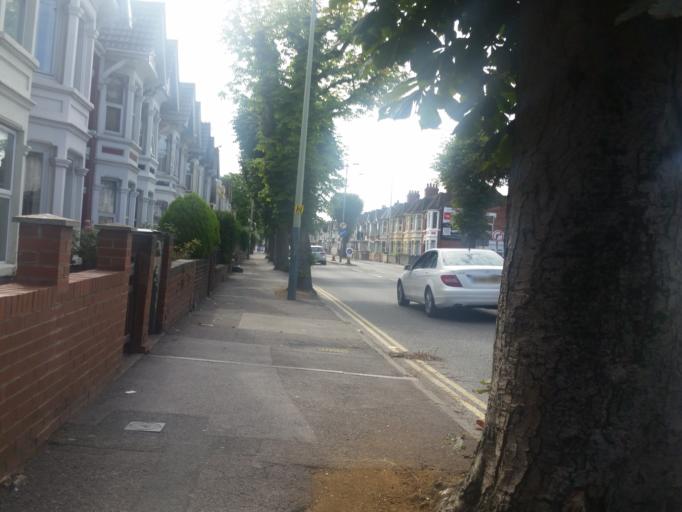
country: GB
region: England
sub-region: Borough of Swindon
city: Swindon
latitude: 51.5657
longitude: -1.7743
